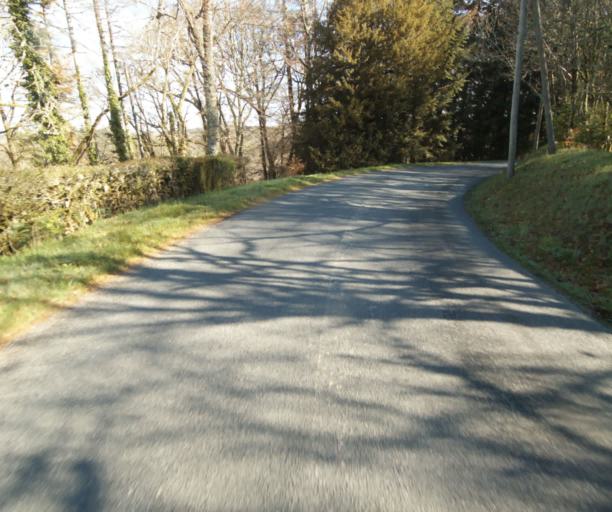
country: FR
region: Limousin
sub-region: Departement de la Correze
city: Correze
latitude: 45.3024
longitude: 1.8686
